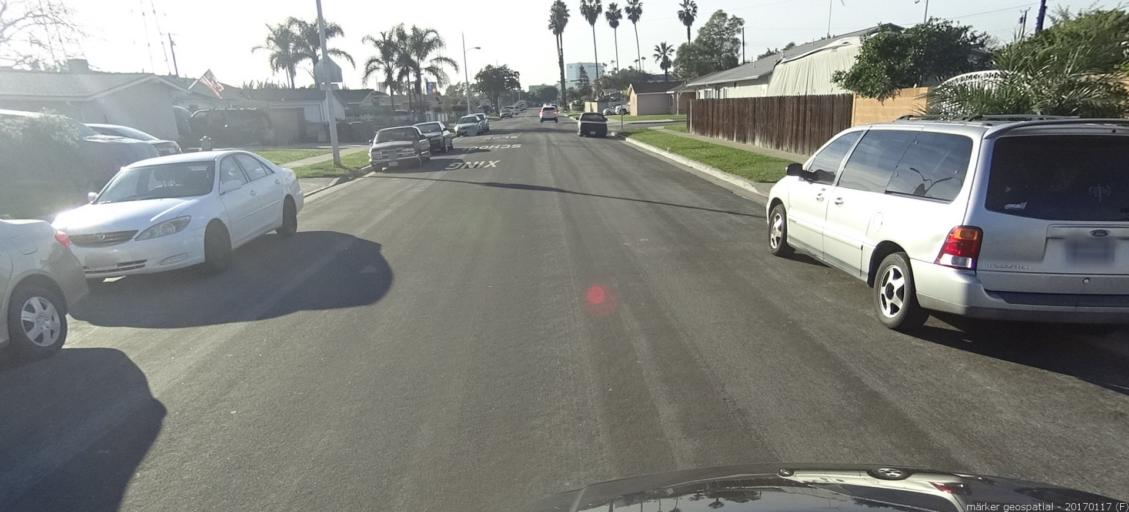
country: US
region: California
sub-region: Orange County
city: Midway City
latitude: 33.7343
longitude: -117.9837
